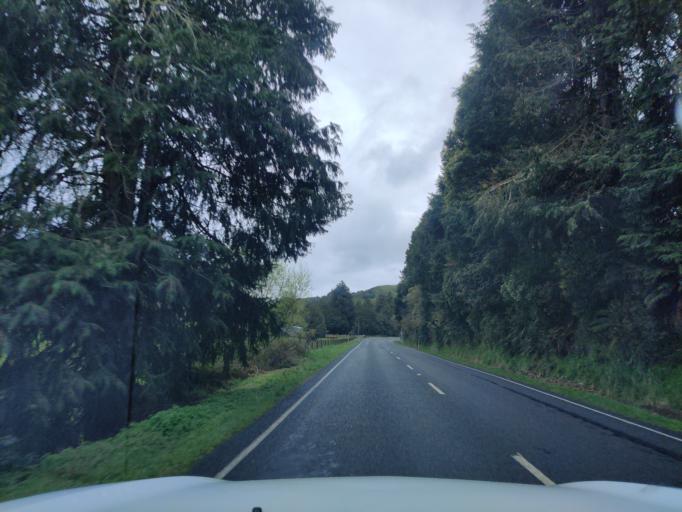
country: NZ
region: Waikato
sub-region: Otorohanga District
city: Otorohanga
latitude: -38.5580
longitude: 175.1953
